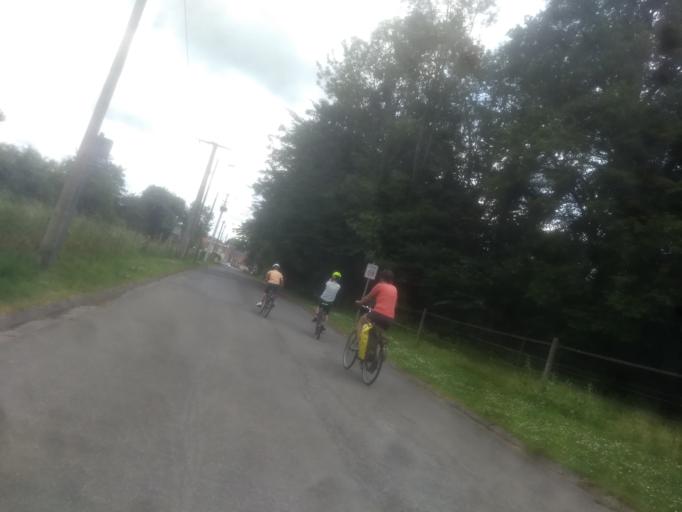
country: FR
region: Nord-Pas-de-Calais
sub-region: Departement du Pas-de-Calais
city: Duisans
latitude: 50.3095
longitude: 2.6548
